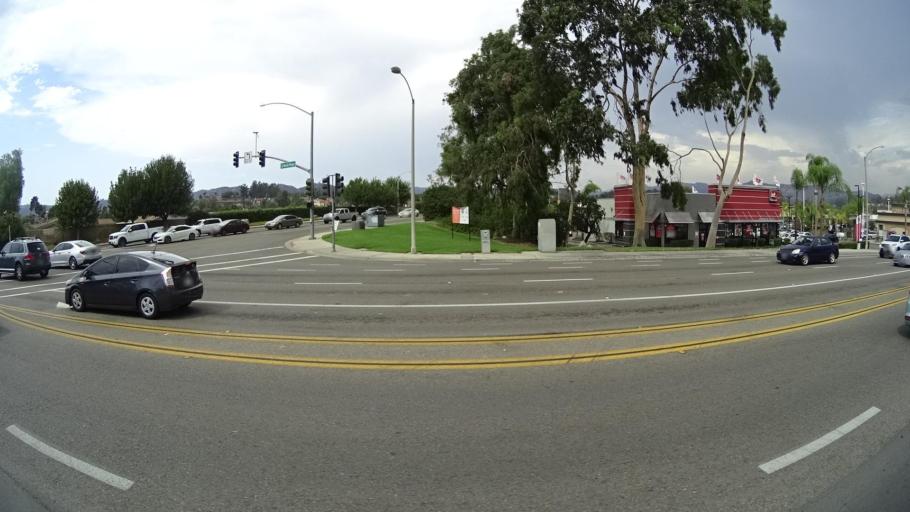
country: US
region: California
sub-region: San Diego County
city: Escondido
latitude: 33.1470
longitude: -117.1084
